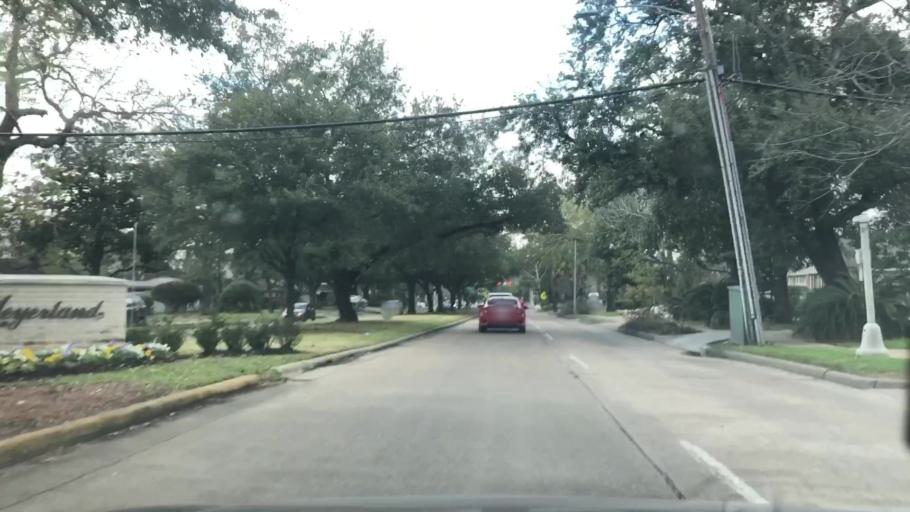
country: US
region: Texas
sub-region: Harris County
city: Bellaire
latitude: 29.6893
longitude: -95.4653
